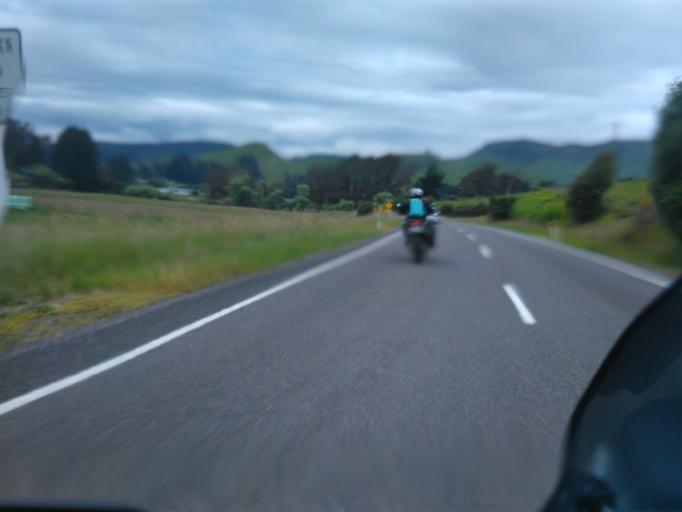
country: NZ
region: Bay of Plenty
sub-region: Opotiki District
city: Opotiki
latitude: -38.3604
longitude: 177.5258
